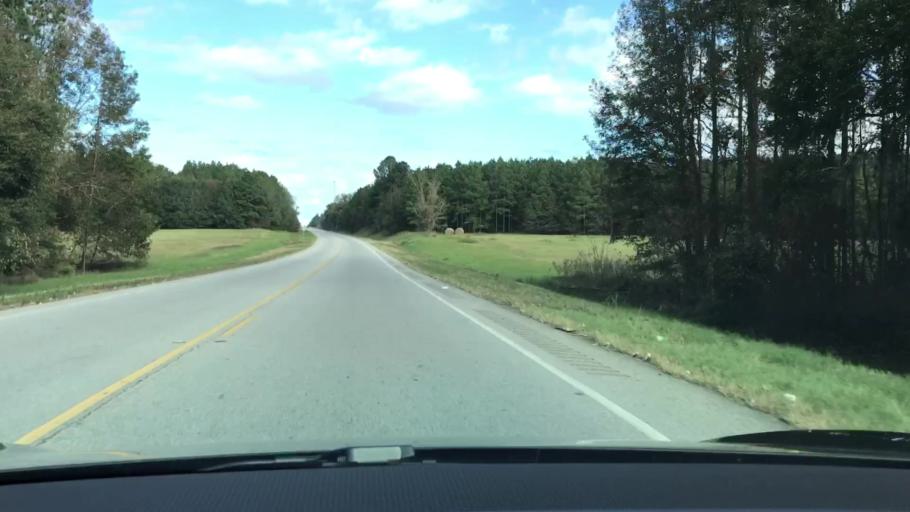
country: US
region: Georgia
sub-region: Jefferson County
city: Wadley
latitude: 32.8956
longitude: -82.4008
